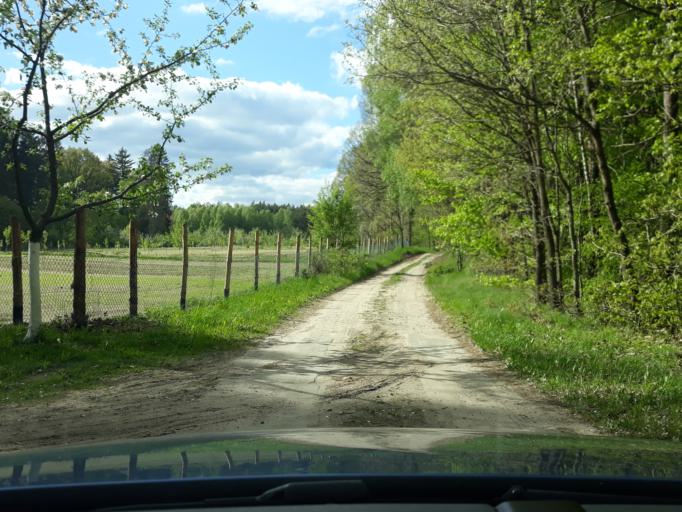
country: PL
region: Pomeranian Voivodeship
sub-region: Powiat czluchowski
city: Czluchow
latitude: 53.7470
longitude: 17.3337
